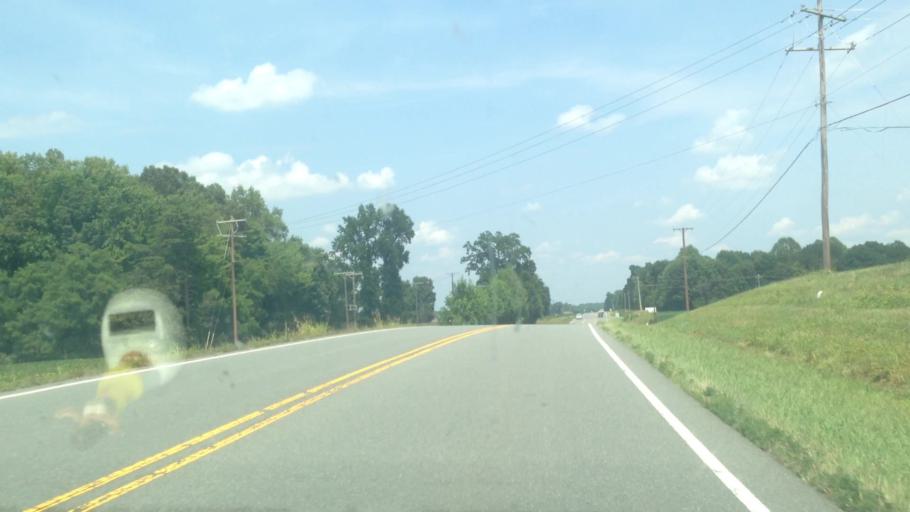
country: US
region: North Carolina
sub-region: Forsyth County
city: Walkertown
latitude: 36.1899
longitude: -80.1058
